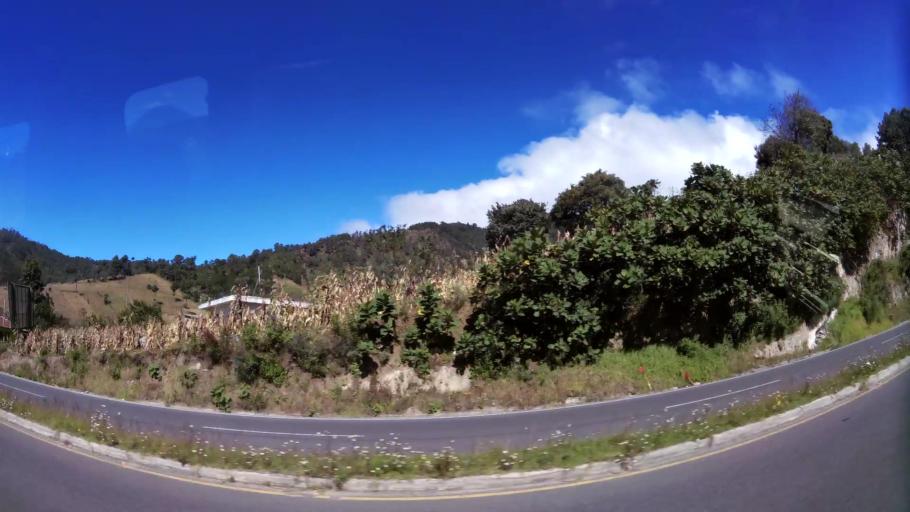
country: GT
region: Solola
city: Solola
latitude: 14.8275
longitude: -91.1930
